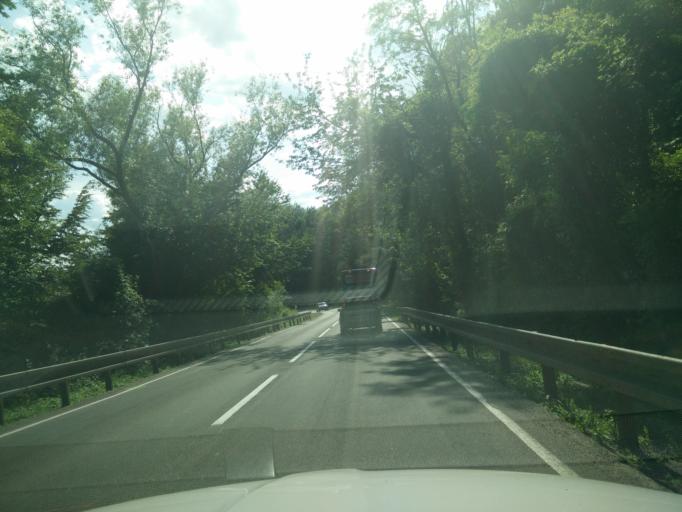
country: SK
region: Nitriansky
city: Prievidza
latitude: 48.8953
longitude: 18.6951
